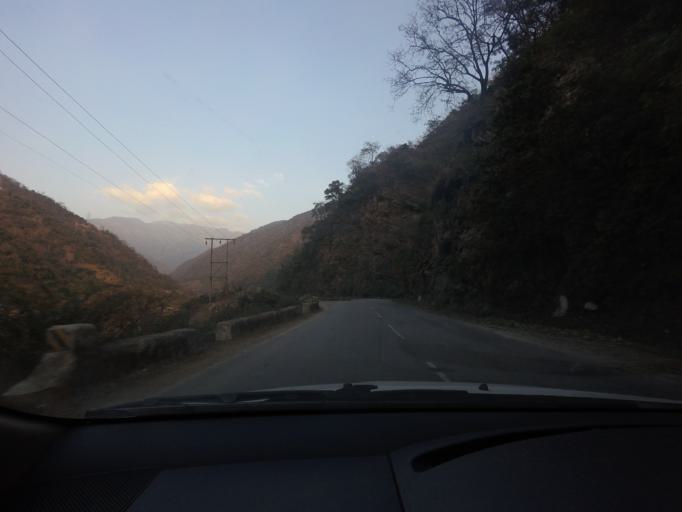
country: IN
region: Himachal Pradesh
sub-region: Mandi
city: Mandi
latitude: 31.7081
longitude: 76.9834
